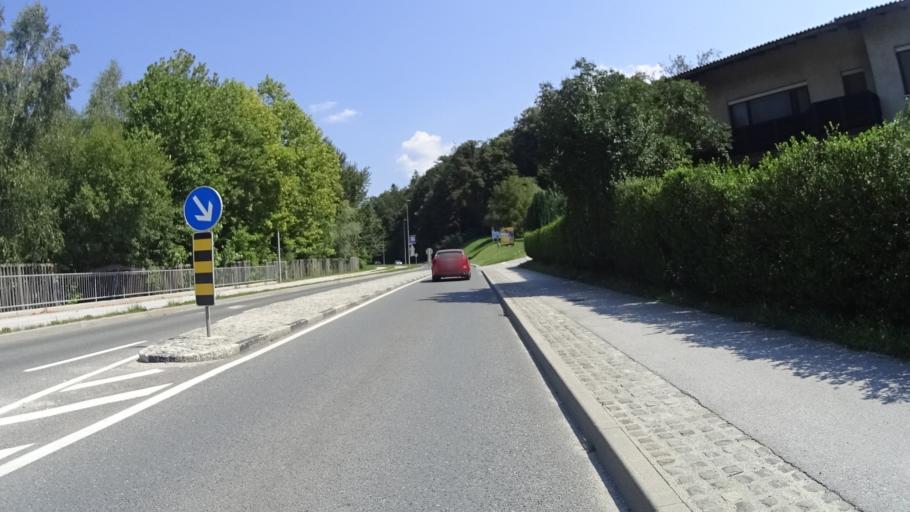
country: SI
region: Ravne na Koroskem
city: Ravne na Koroskem
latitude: 46.5428
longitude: 14.9516
